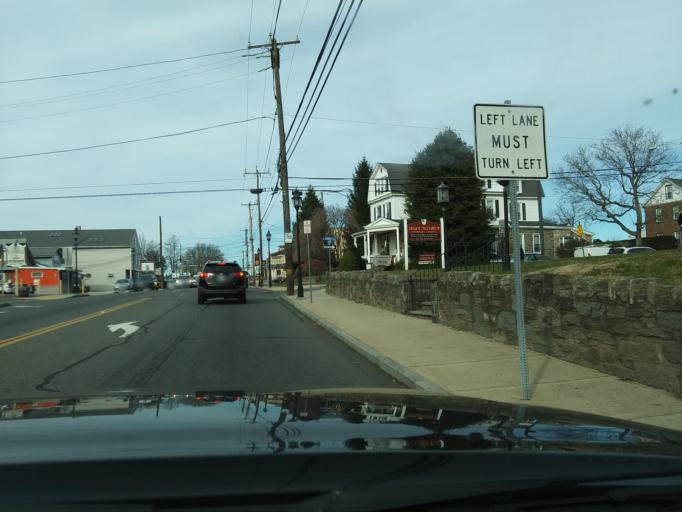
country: US
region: Pennsylvania
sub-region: Montgomery County
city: Rockledge
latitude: 40.0803
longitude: -75.0887
